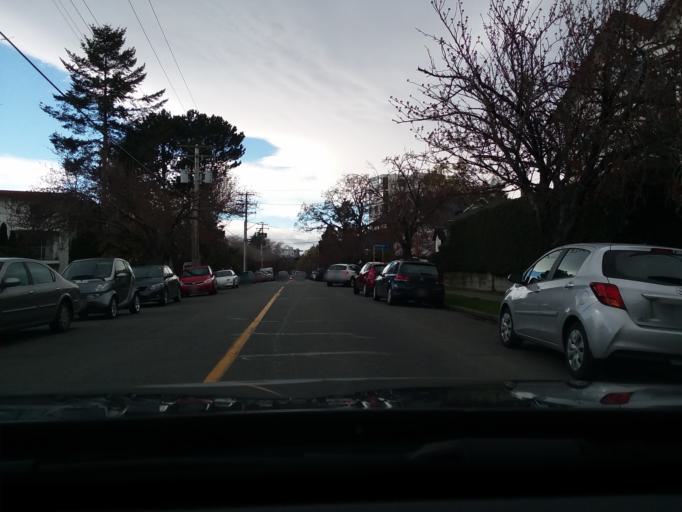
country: CA
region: British Columbia
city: Victoria
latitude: 48.4163
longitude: -123.3503
